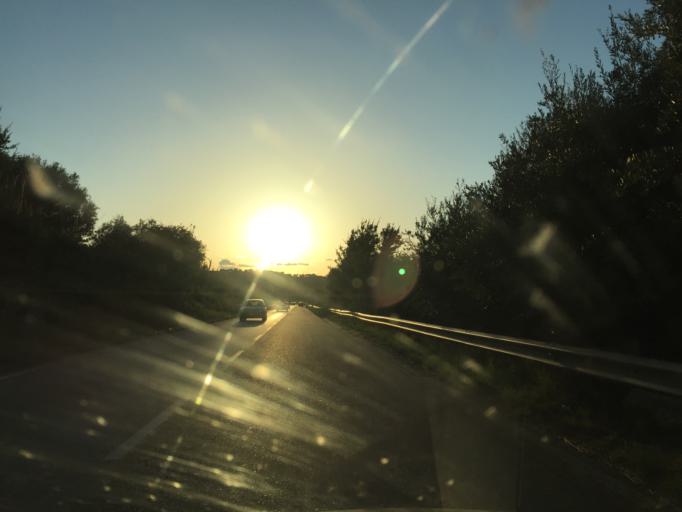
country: IT
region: Calabria
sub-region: Provincia di Vibo-Valentia
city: Pannaconi
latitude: 38.7170
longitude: 16.0530
